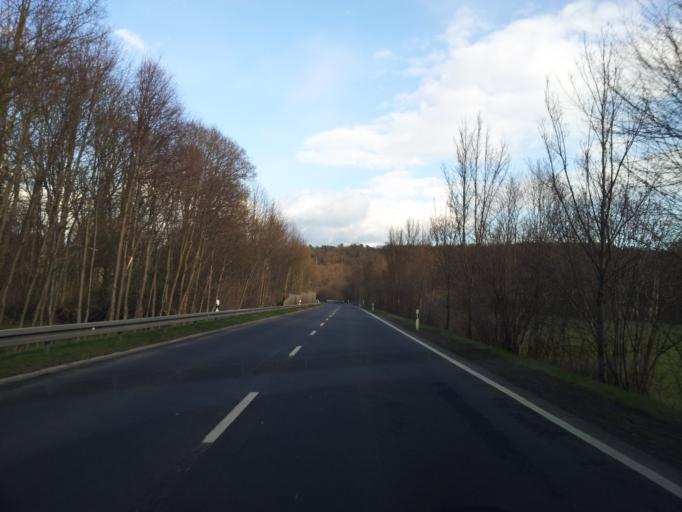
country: DE
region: Saxony
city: Konigsbruck
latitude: 51.2614
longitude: 13.9058
